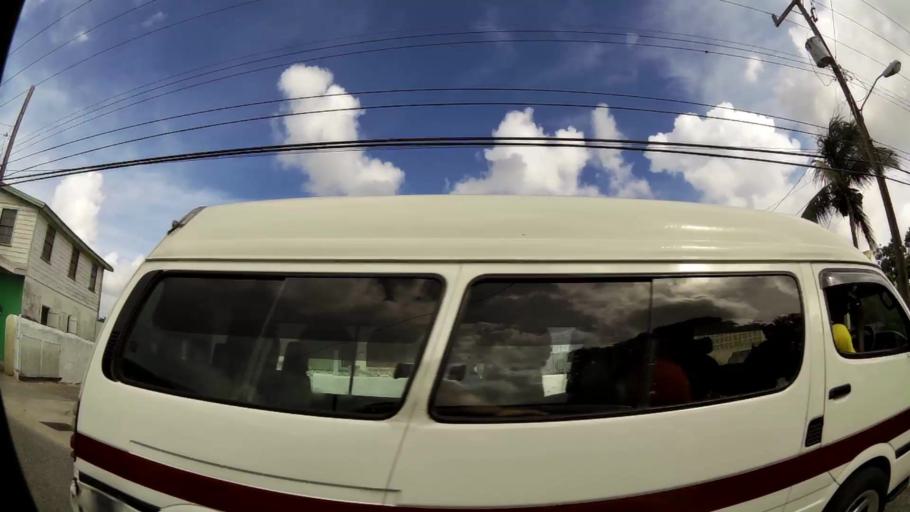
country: BB
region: Saint Michael
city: Bridgetown
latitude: 13.1281
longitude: -59.6066
